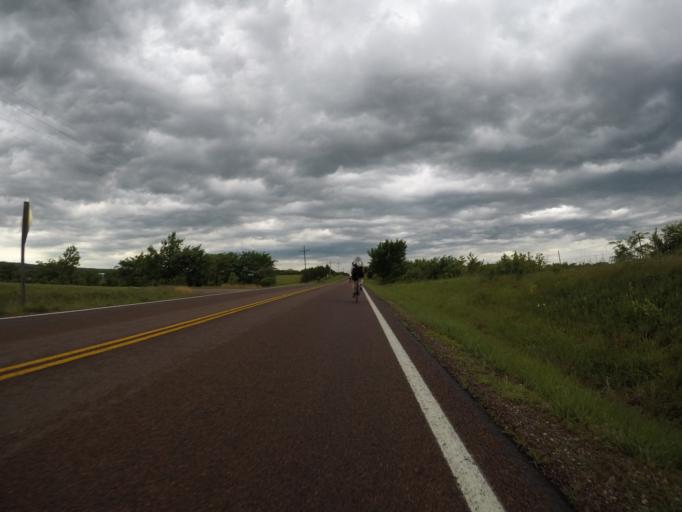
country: US
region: Kansas
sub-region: Shawnee County
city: Rossville
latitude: 38.9645
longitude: -95.9853
